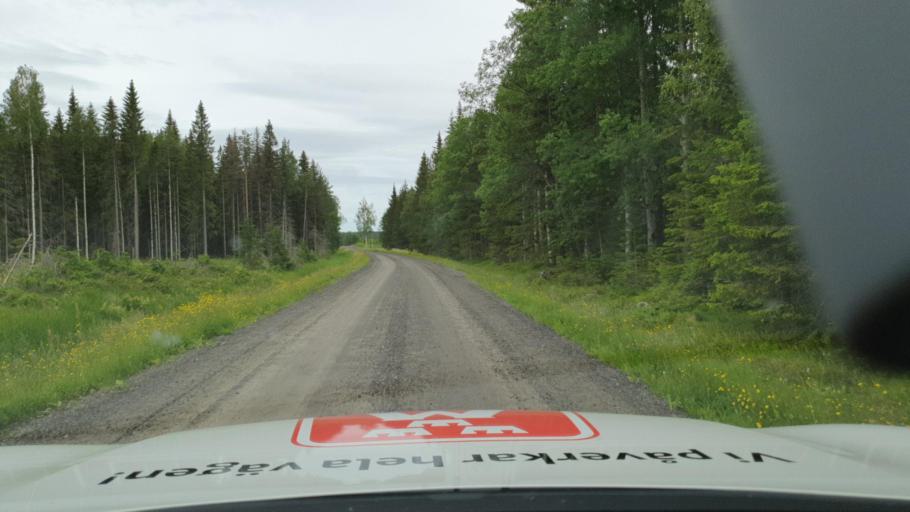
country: SE
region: Vaesterbotten
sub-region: Skelleftea Kommun
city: Burtraesk
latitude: 64.3836
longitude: 20.6142
